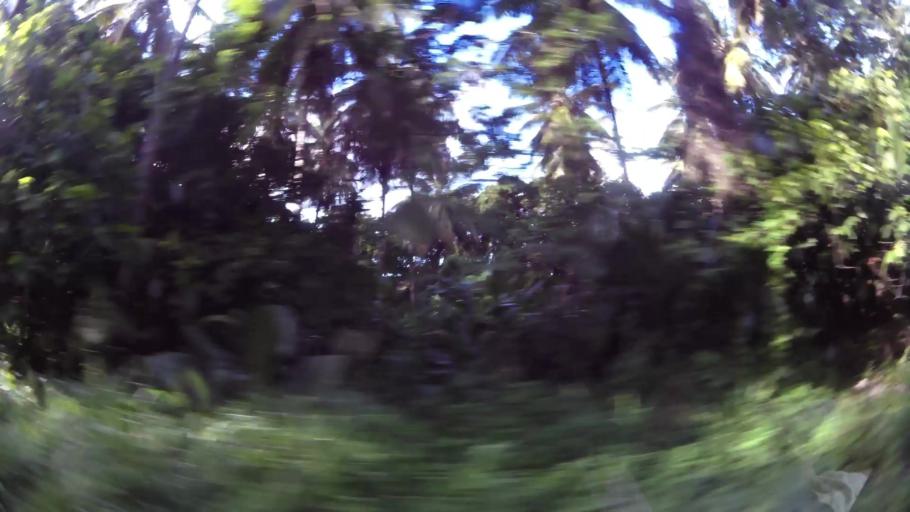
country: DM
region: Saint Joseph
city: Saint Joseph
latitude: 15.3944
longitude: -61.4211
